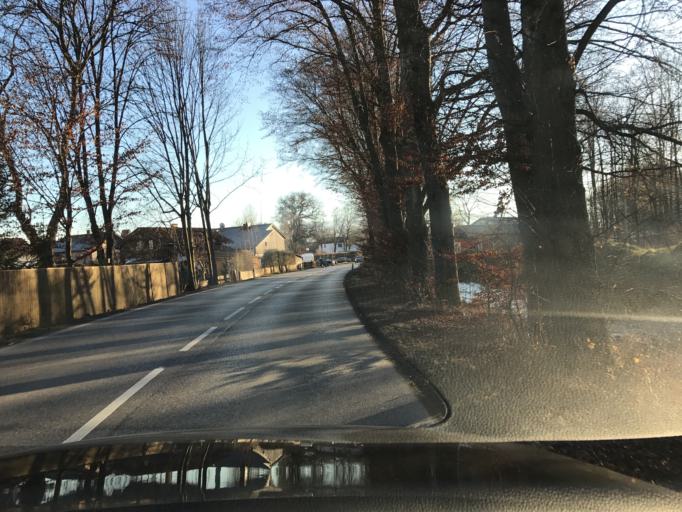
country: DE
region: Bavaria
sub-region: Upper Bavaria
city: Bad Aibling
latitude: 47.8819
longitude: 11.9932
